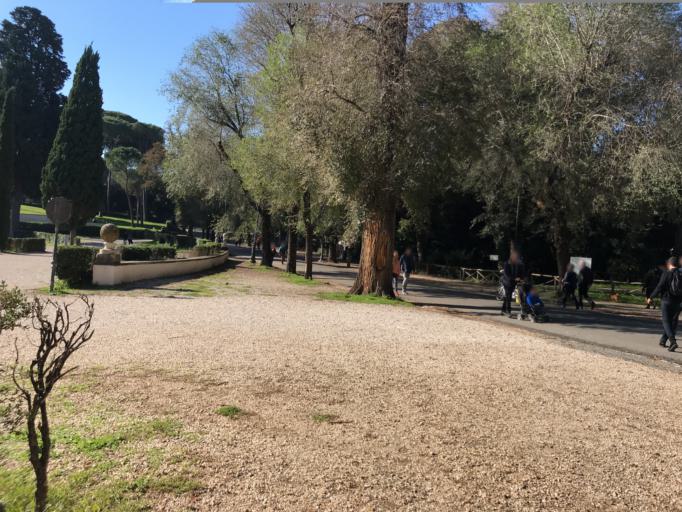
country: IT
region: Latium
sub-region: Citta metropolitana di Roma Capitale
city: Rome
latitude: 41.9145
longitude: 12.4867
